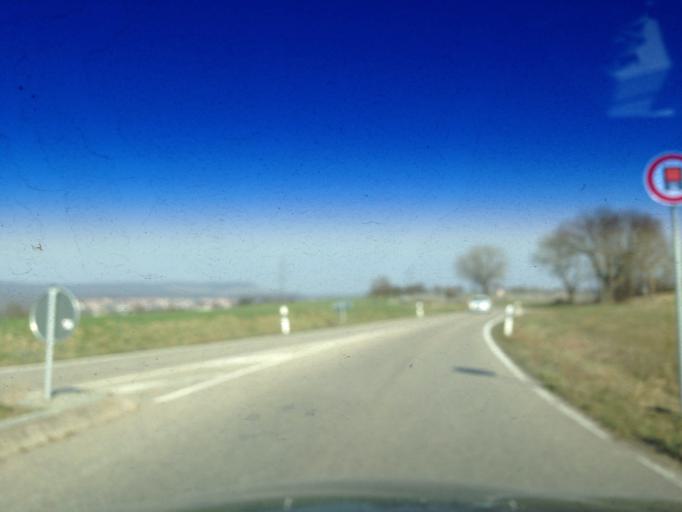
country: DE
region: Baden-Wuerttemberg
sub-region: Karlsruhe Region
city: Illingen
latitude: 48.9469
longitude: 8.8915
